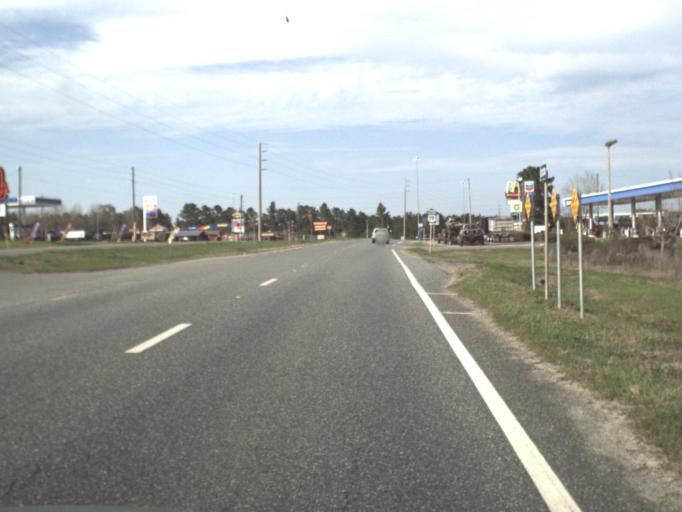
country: US
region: Florida
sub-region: Jefferson County
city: Monticello
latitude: 30.4706
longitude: -83.8913
